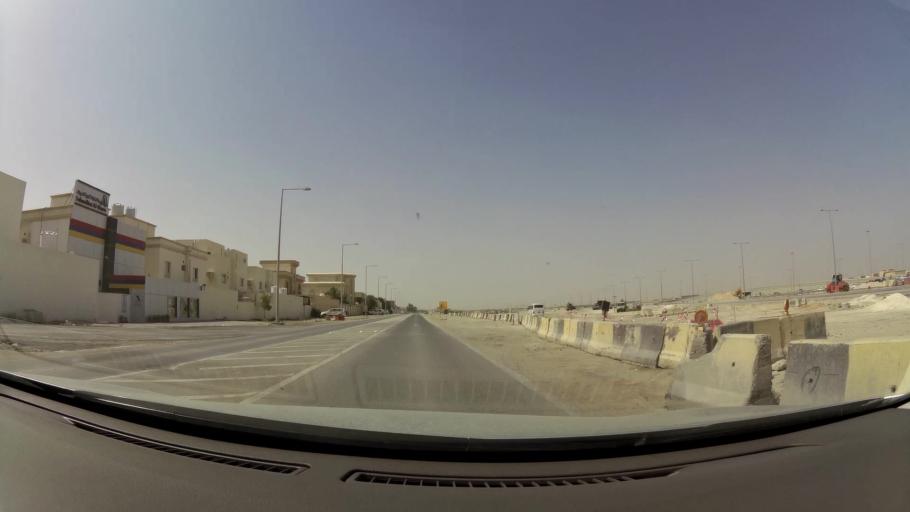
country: QA
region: Baladiyat Umm Salal
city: Umm Salal Muhammad
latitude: 25.3684
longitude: 51.4442
